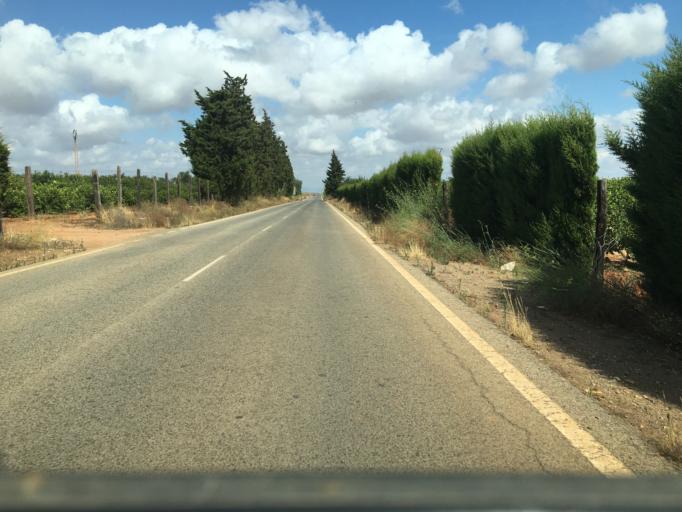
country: ES
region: Murcia
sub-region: Murcia
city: La Union
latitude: 37.6458
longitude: -0.8738
